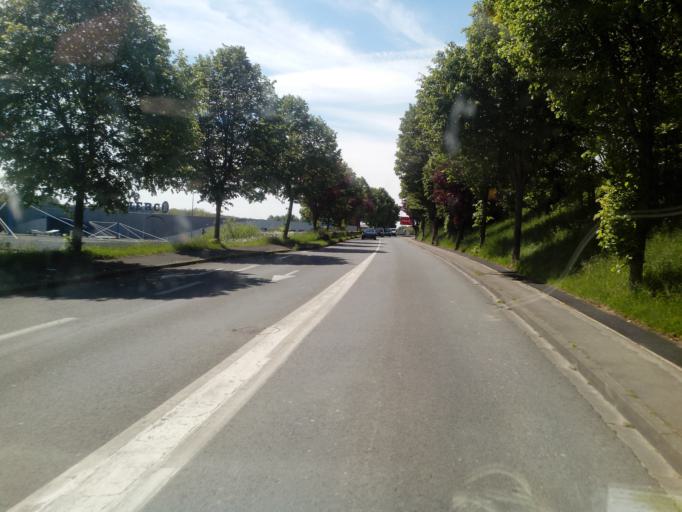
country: FR
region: Nord-Pas-de-Calais
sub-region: Departement du Pas-de-Calais
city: Montreuil
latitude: 50.4829
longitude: 1.7591
